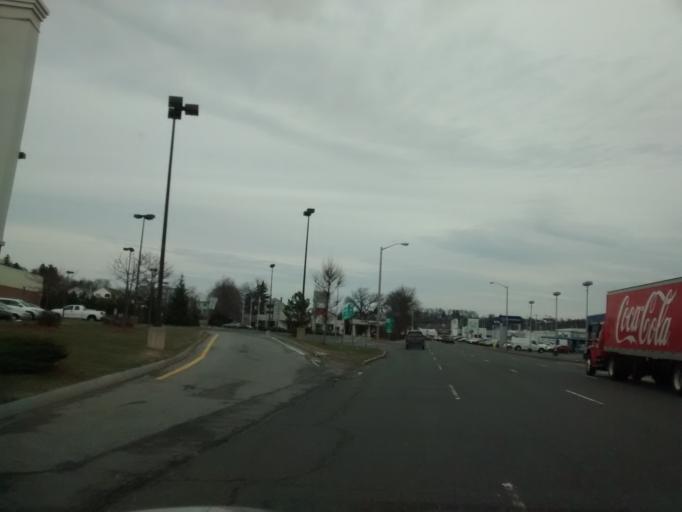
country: US
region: Massachusetts
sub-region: Worcester County
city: Worcester
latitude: 42.2875
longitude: -71.8058
